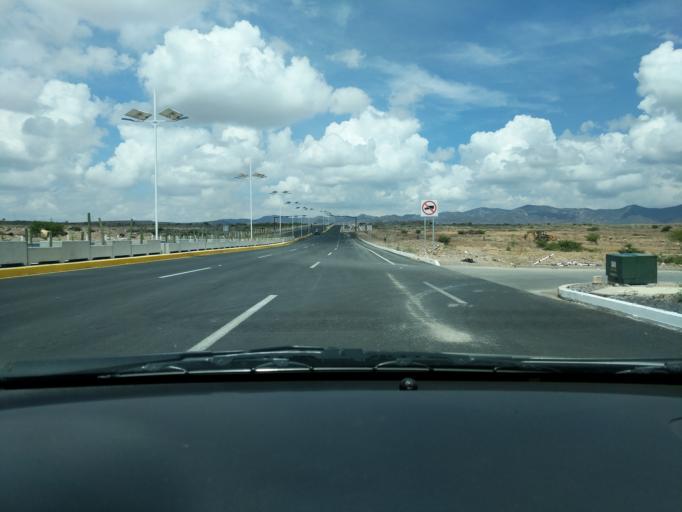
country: MX
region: San Luis Potosi
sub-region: Mexquitic de Carmona
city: Guadalupe Victoria
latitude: 22.1664
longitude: -101.0508
